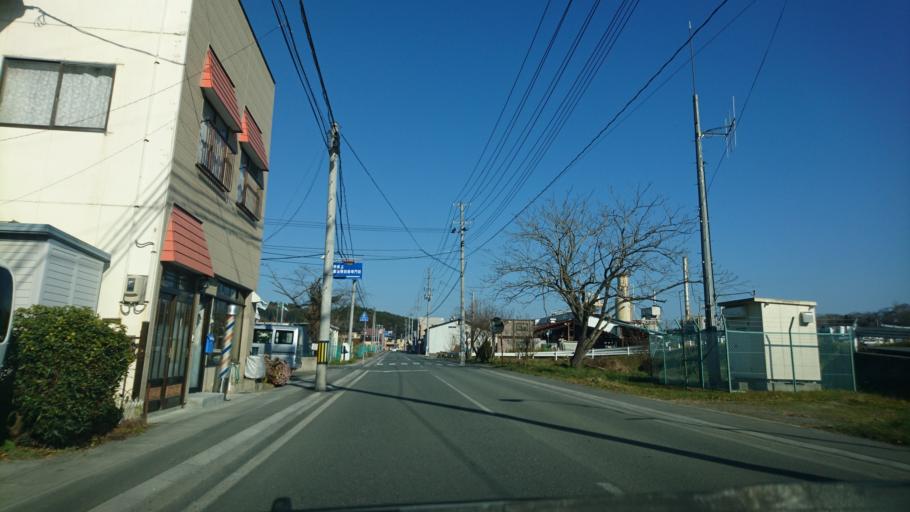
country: JP
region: Iwate
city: Ichinoseki
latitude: 38.9144
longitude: 141.3282
